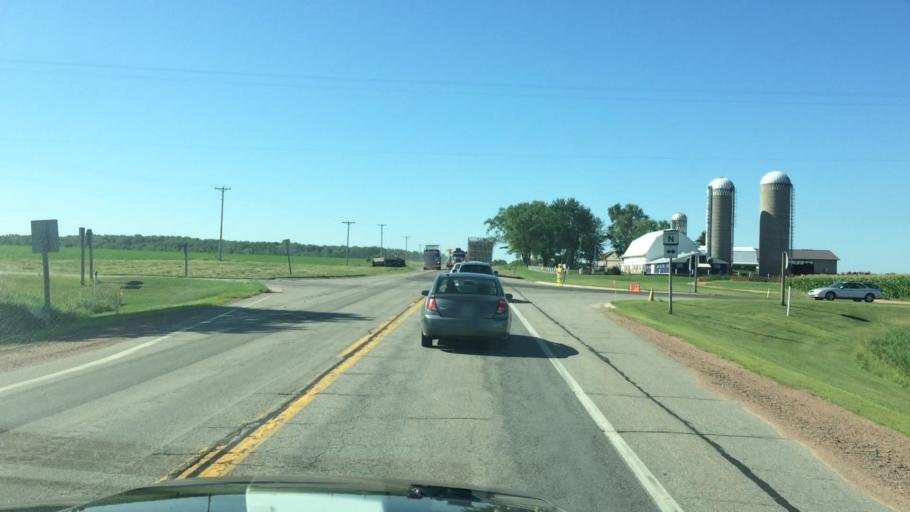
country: US
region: Wisconsin
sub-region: Marathon County
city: Stratford
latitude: 44.9026
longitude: -90.0787
